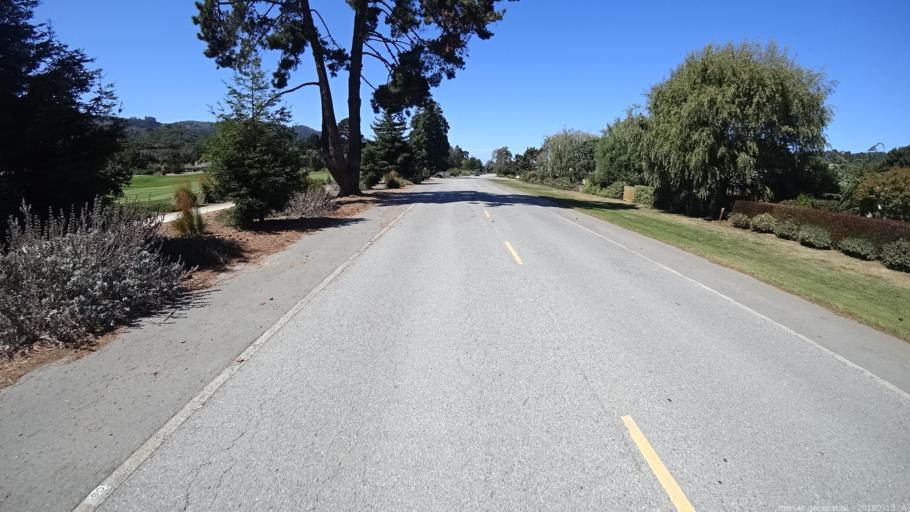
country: US
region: California
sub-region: Monterey County
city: Carmel-by-the-Sea
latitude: 36.5328
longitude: -121.8649
